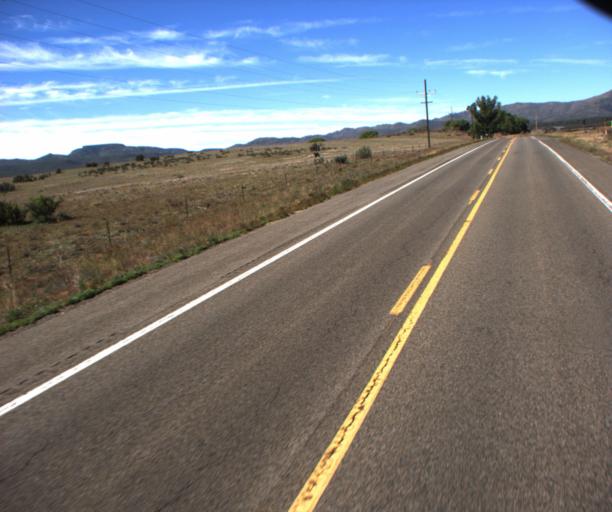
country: US
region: Arizona
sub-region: Yavapai County
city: Congress
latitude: 34.3030
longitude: -112.7189
